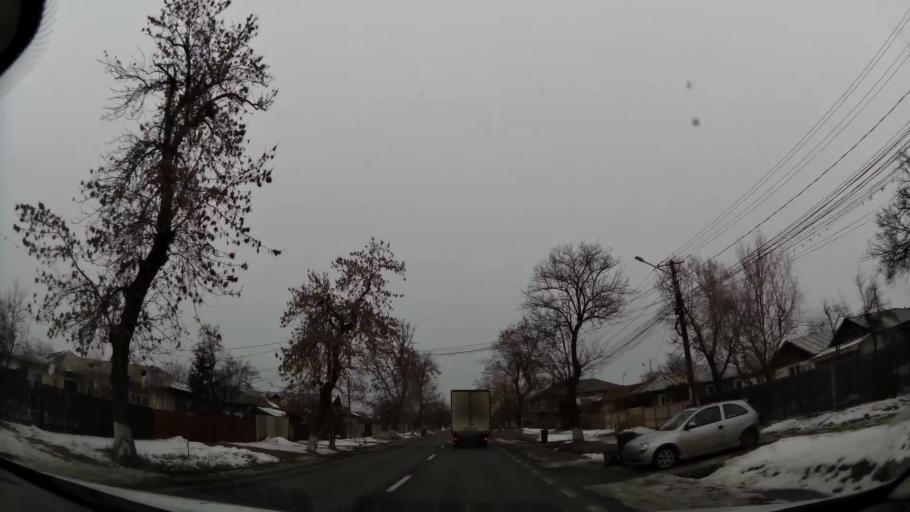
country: RO
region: Dambovita
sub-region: Comuna Tartasesti
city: Baldana
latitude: 44.6099
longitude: 25.7673
